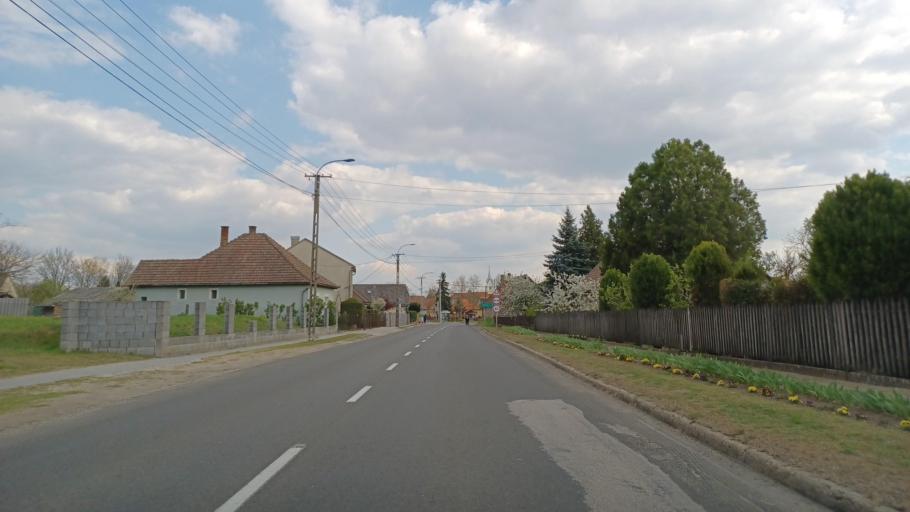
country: HU
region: Fejer
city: Cece
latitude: 46.7192
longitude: 18.6638
